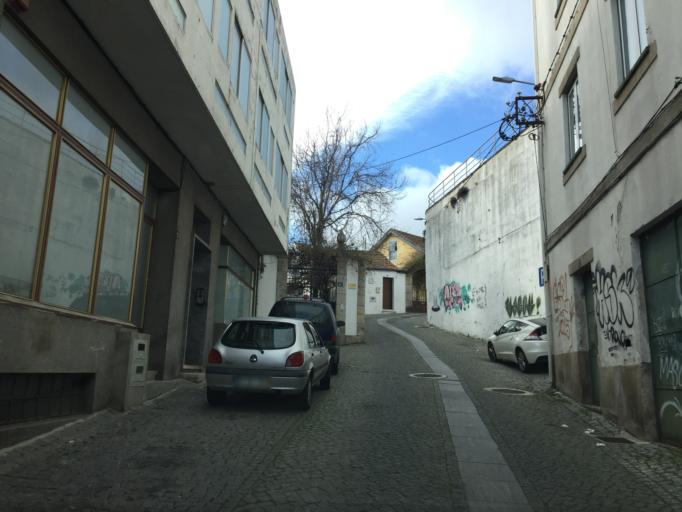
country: PT
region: Castelo Branco
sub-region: Covilha
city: Covilha
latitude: 40.2790
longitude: -7.5041
